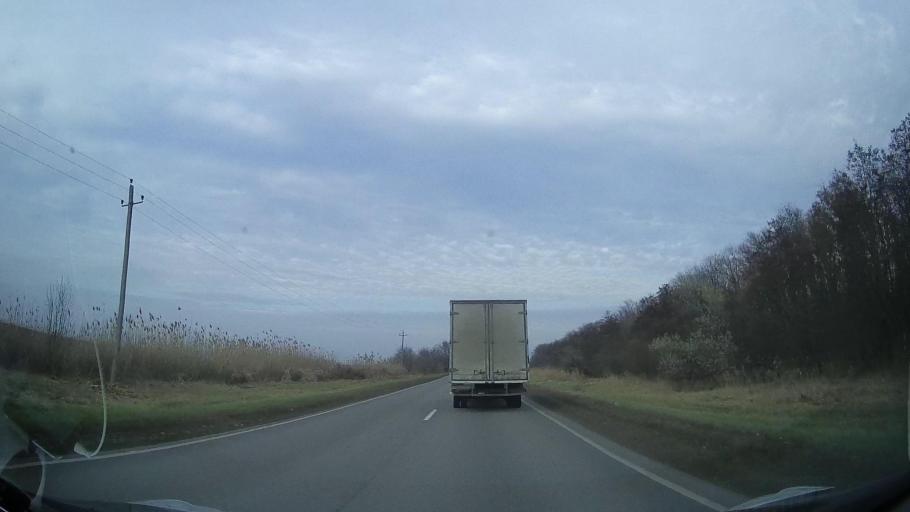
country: RU
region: Rostov
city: Ol'ginskaya
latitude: 47.1494
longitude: 39.9109
